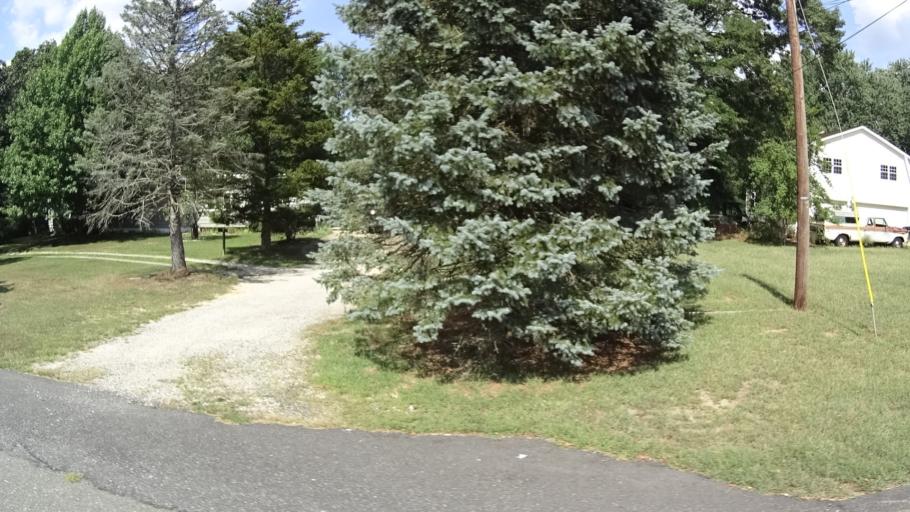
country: US
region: New Jersey
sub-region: Monmouth County
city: Ramtown
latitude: 40.1556
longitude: -74.1158
